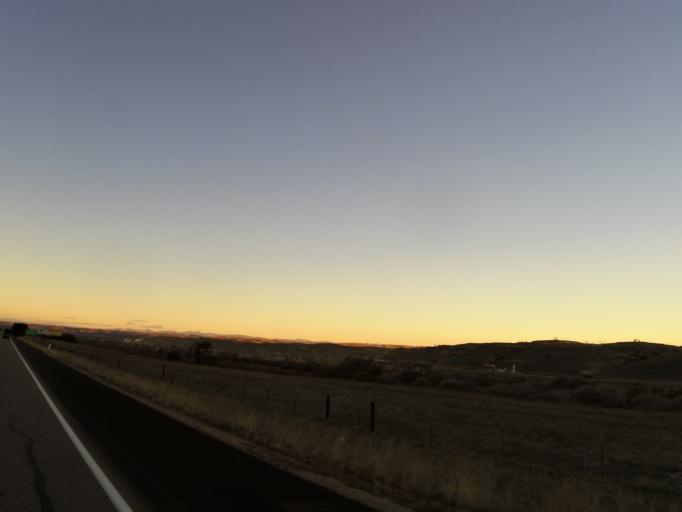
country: US
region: California
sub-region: San Luis Obispo County
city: Lake Nacimiento
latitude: 35.9321
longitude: -120.8708
